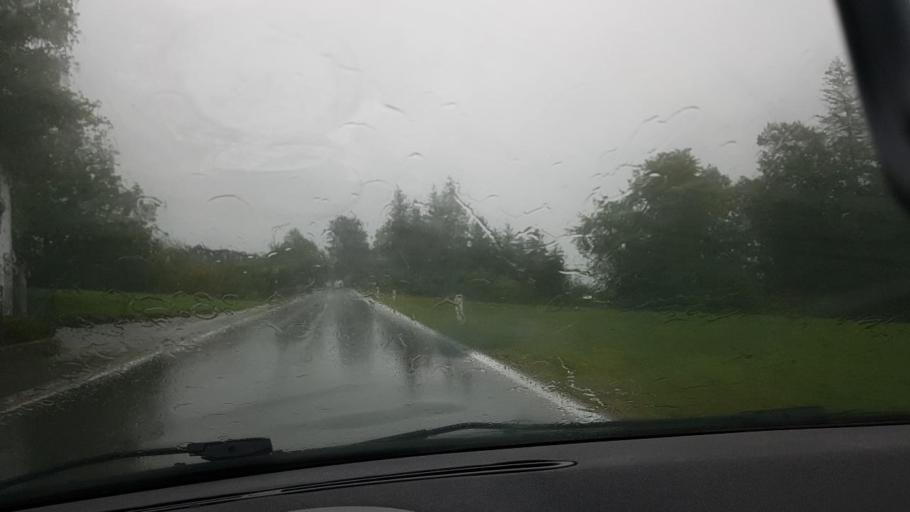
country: AT
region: Vorarlberg
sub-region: Politischer Bezirk Bludenz
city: Innerbraz
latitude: 47.1468
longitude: 9.8899
